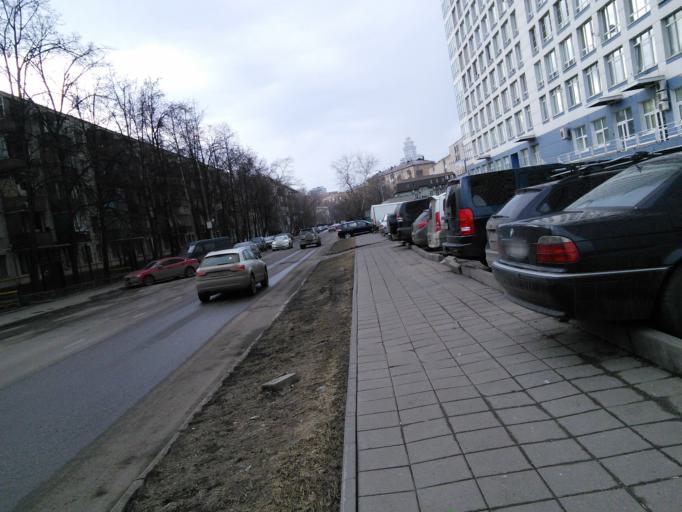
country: RU
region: Moscow
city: Sokol
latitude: 55.8062
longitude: 37.5458
